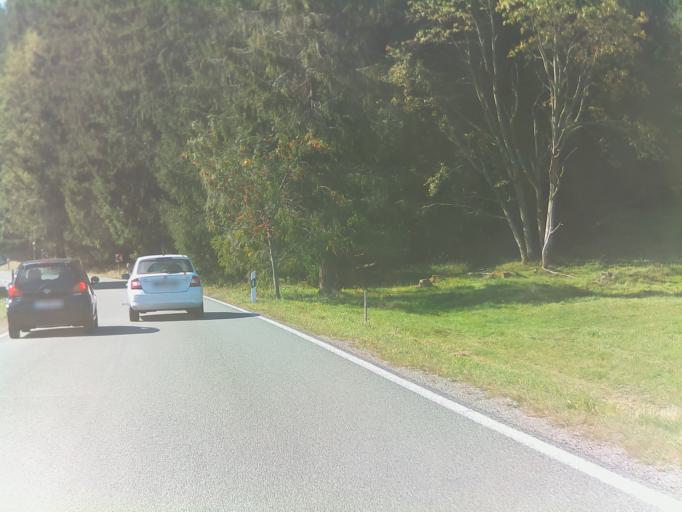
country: DE
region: Thuringia
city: Frauenwald
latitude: 50.6037
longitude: 10.8618
